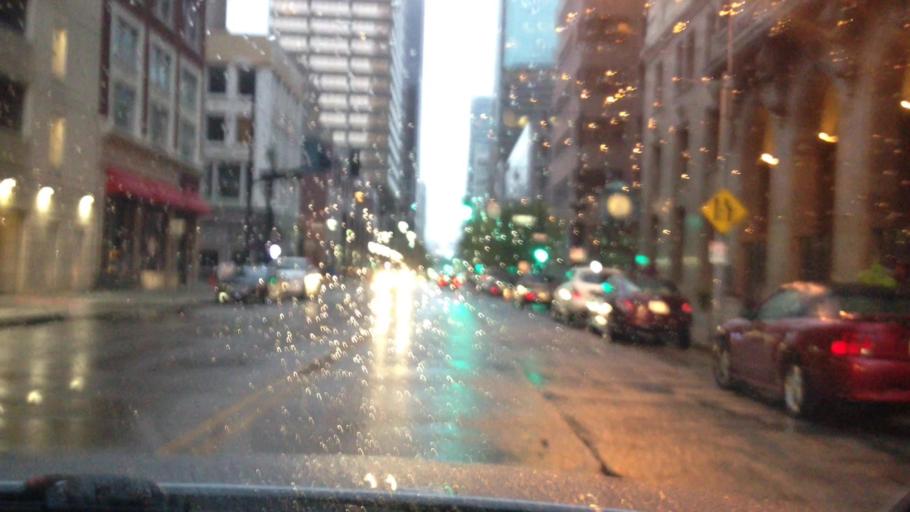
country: US
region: Missouri
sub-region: Jackson County
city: Kansas City
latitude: 39.1029
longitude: -94.5820
